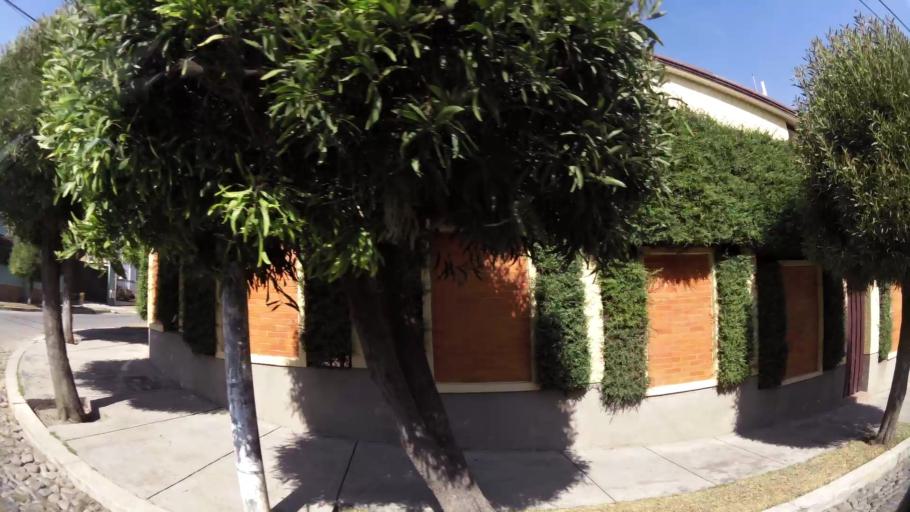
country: BO
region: La Paz
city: La Paz
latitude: -16.5347
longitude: -68.0736
